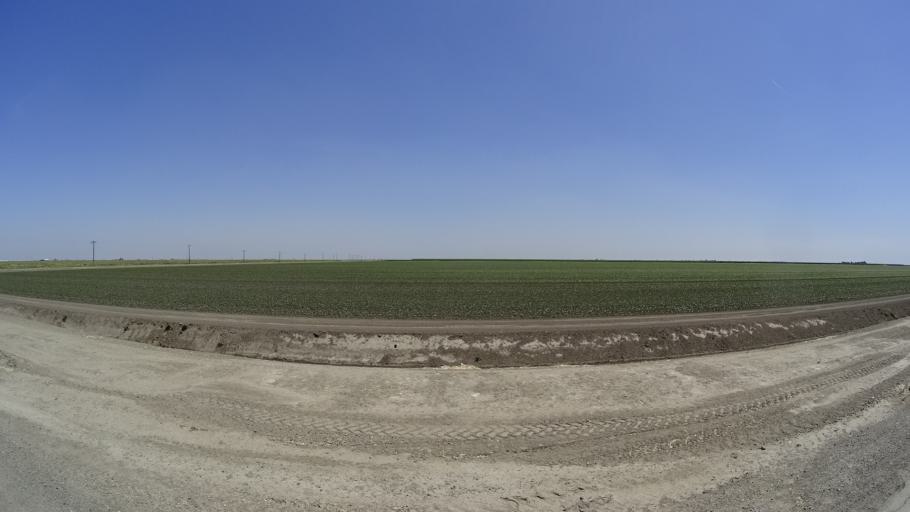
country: US
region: California
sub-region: Kings County
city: Corcoran
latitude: 36.1367
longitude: -119.6444
